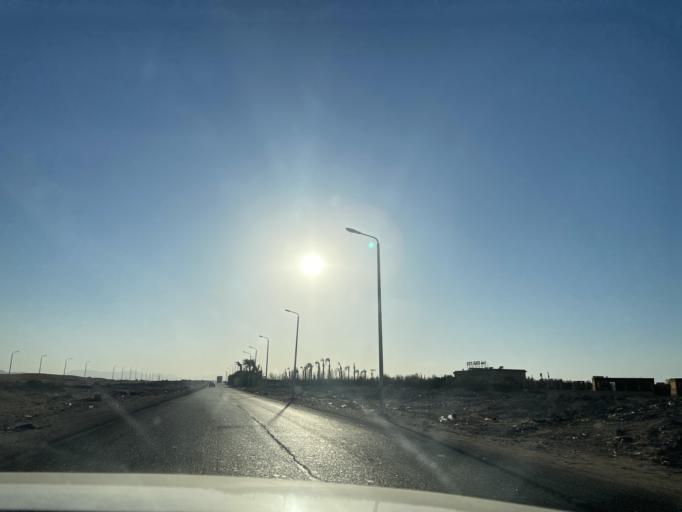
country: EG
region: Red Sea
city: Hurghada
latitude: 27.2176
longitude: 33.7969
